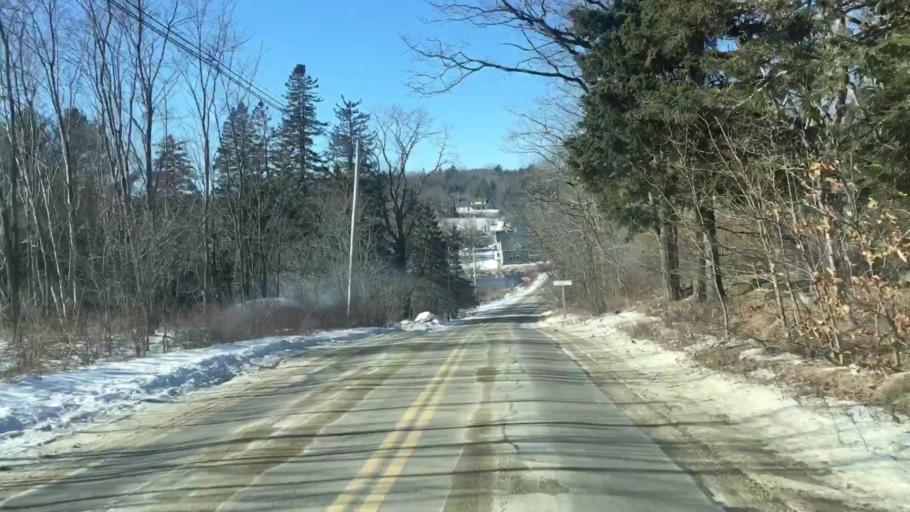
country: US
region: Maine
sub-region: Hancock County
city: Sedgwick
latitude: 44.3451
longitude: -68.6806
